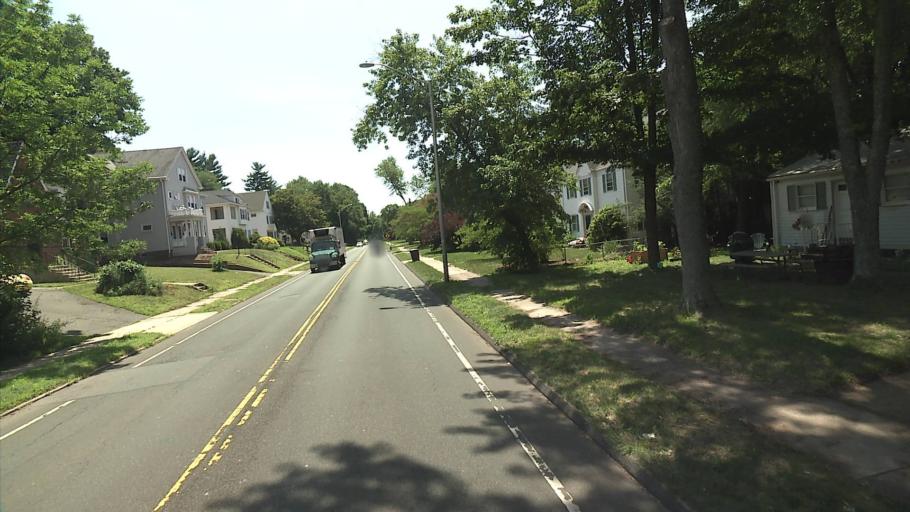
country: US
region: Connecticut
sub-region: Hartford County
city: New Britain
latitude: 41.6584
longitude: -72.8004
